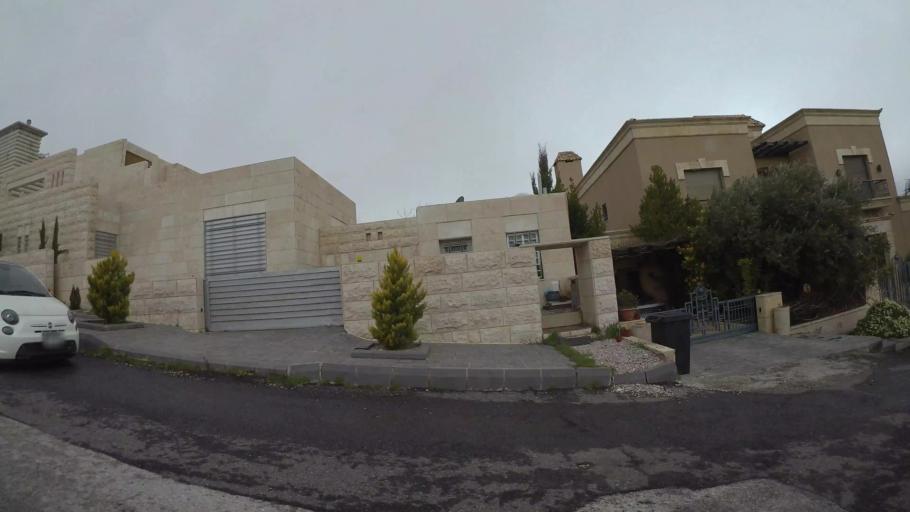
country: JO
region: Amman
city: Umm as Summaq
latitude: 31.9133
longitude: 35.8651
